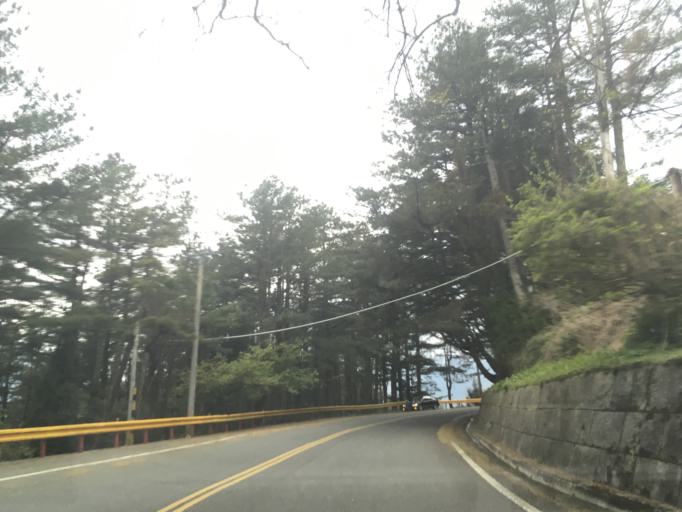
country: TW
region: Taiwan
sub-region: Hualien
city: Hualian
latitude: 24.1829
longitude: 121.3267
